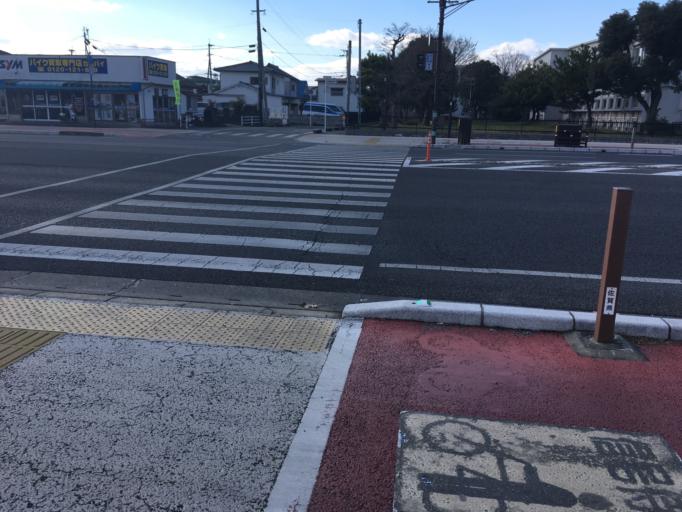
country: JP
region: Saga Prefecture
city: Saga-shi
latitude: 33.2414
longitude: 130.2943
